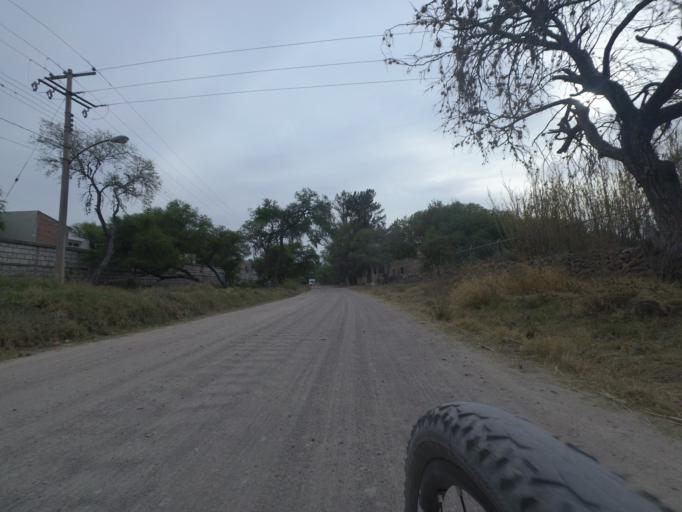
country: MX
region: Aguascalientes
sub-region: Aguascalientes
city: La Loma de los Negritos
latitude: 21.8537
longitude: -102.3566
